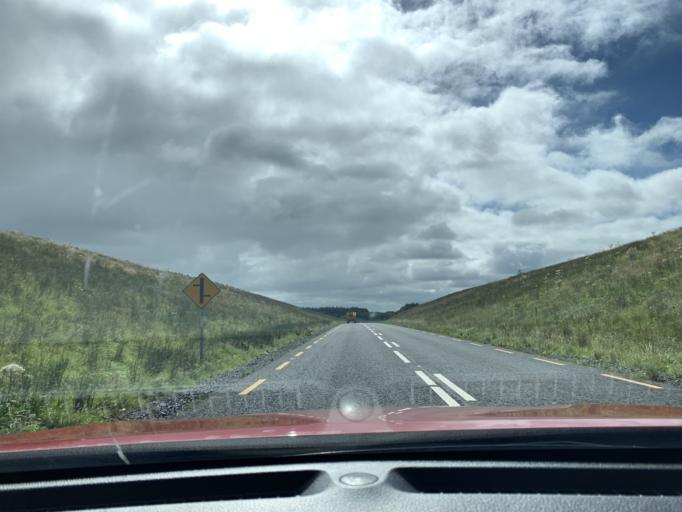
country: IE
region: Connaught
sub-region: Roscommon
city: Boyle
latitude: 53.8993
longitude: -8.2546
